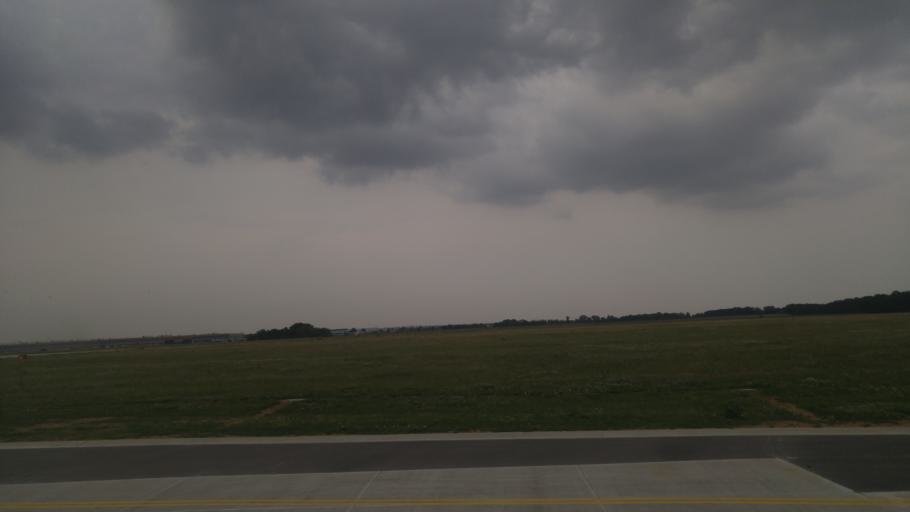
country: CZ
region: Central Bohemia
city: Jenec
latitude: 50.1006
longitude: 14.2296
